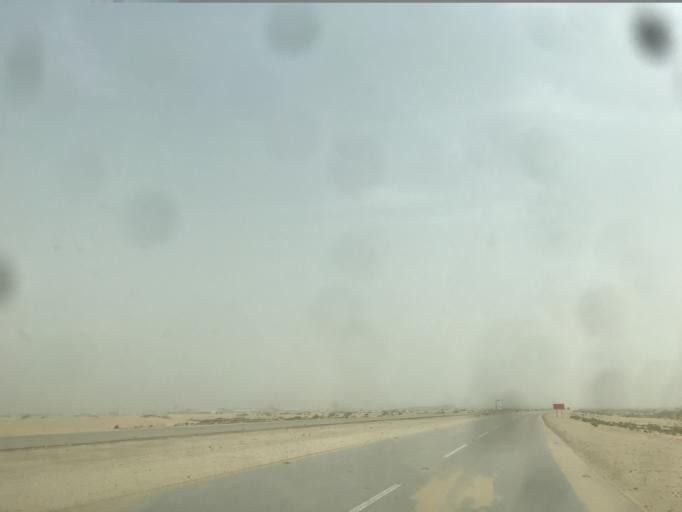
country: SA
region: Eastern Province
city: Abqaiq
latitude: 25.9080
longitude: 49.9251
